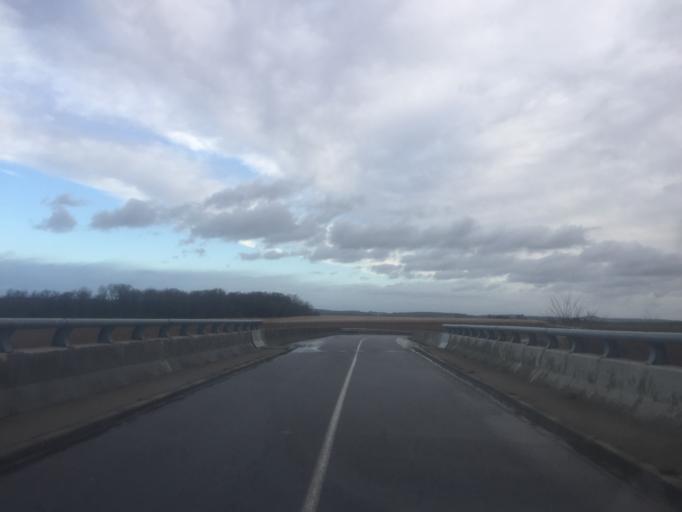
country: FR
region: Franche-Comte
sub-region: Departement de la Haute-Saone
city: Pesmes
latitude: 47.2367
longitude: 5.5925
